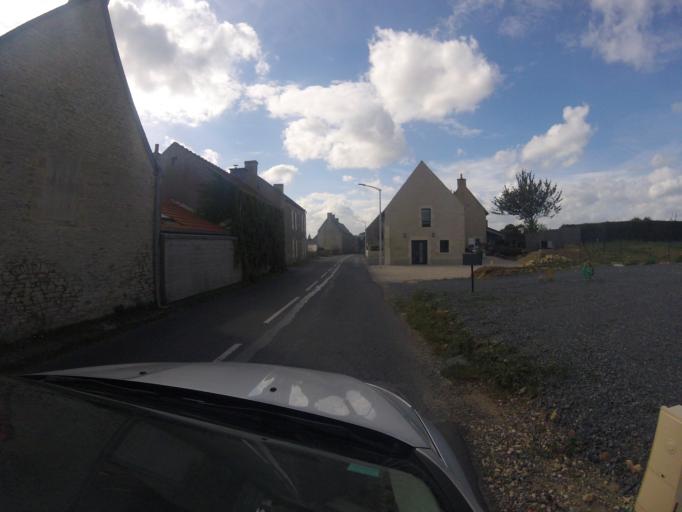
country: FR
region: Lower Normandy
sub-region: Departement du Calvados
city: Saint-Vigor-le-Grand
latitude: 49.3355
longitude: -0.6942
